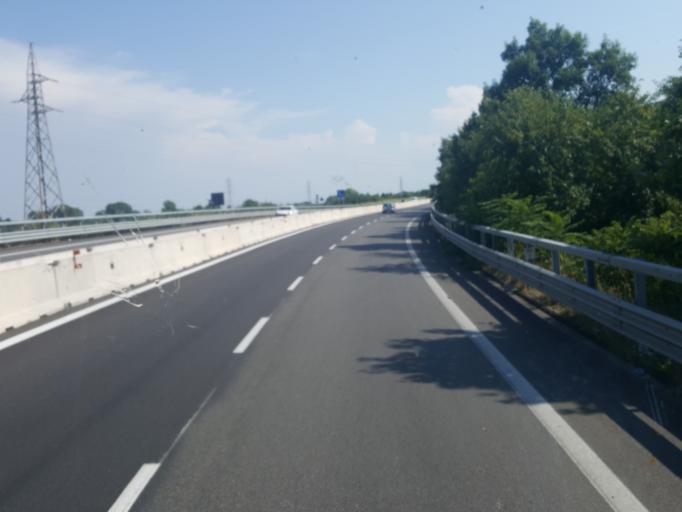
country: IT
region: Lombardy
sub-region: Citta metropolitana di Milano
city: Opera
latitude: 45.3779
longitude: 9.2268
